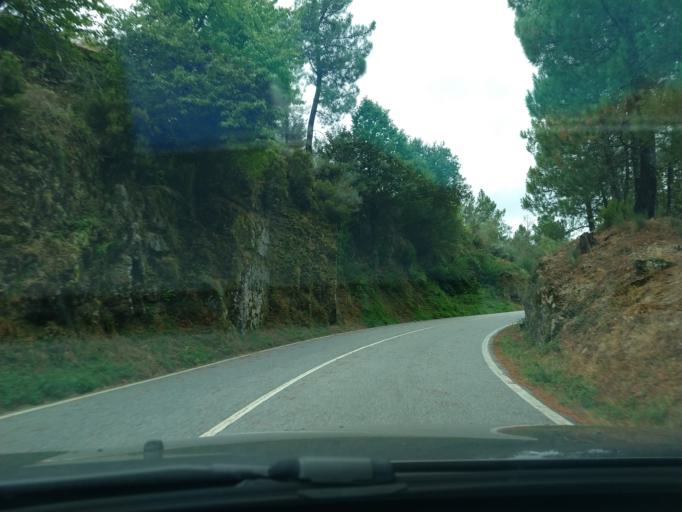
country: PT
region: Guarda
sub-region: Seia
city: Seia
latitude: 40.3236
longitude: -7.6794
